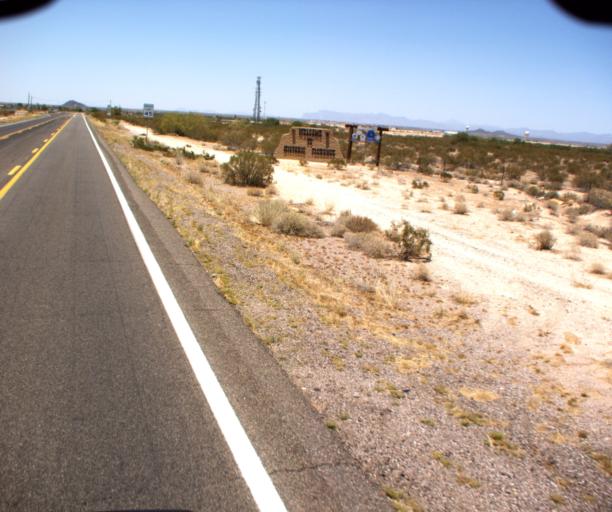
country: US
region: Arizona
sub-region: Pinal County
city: Florence
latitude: 33.0063
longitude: -111.3742
